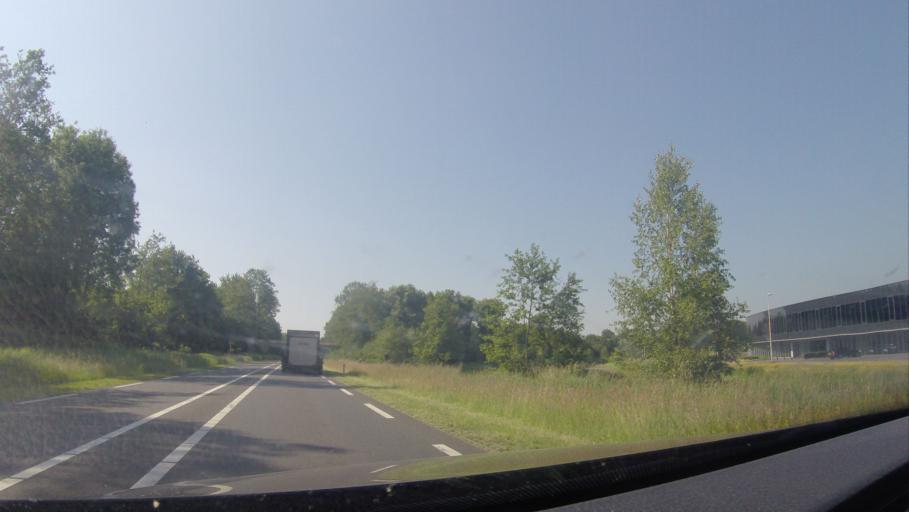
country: NL
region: Gelderland
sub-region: Gemeente Lochem
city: Laren
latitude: 52.2735
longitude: 6.4027
